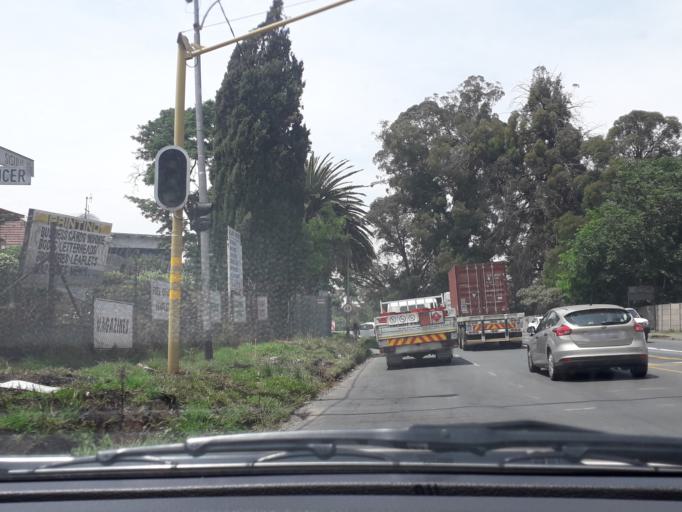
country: ZA
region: Gauteng
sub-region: City of Johannesburg Metropolitan Municipality
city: Roodepoort
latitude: -26.1836
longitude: 27.9402
